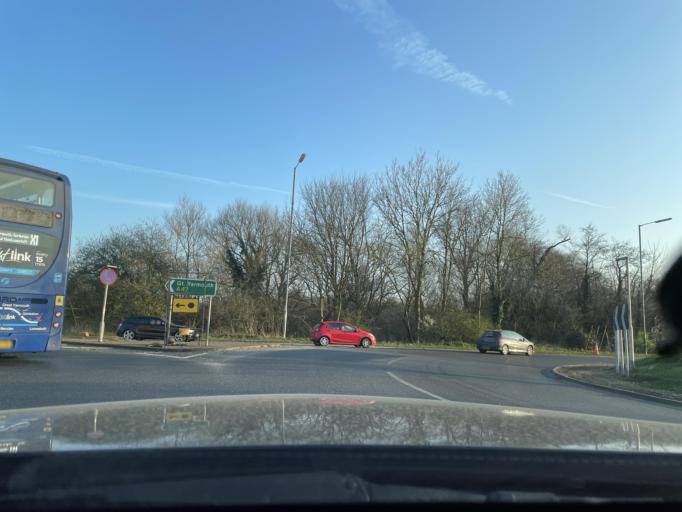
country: GB
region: England
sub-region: Norfolk
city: Acle
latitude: 52.6376
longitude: 1.5547
